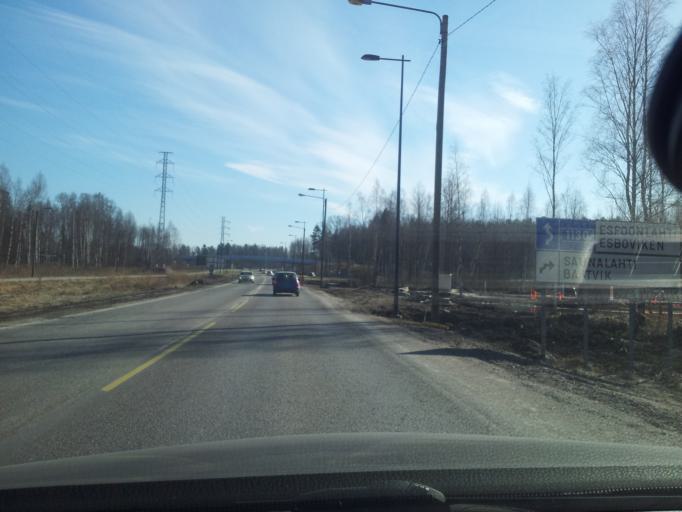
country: FI
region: Uusimaa
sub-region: Helsinki
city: Espoo
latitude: 60.1705
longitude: 24.6181
